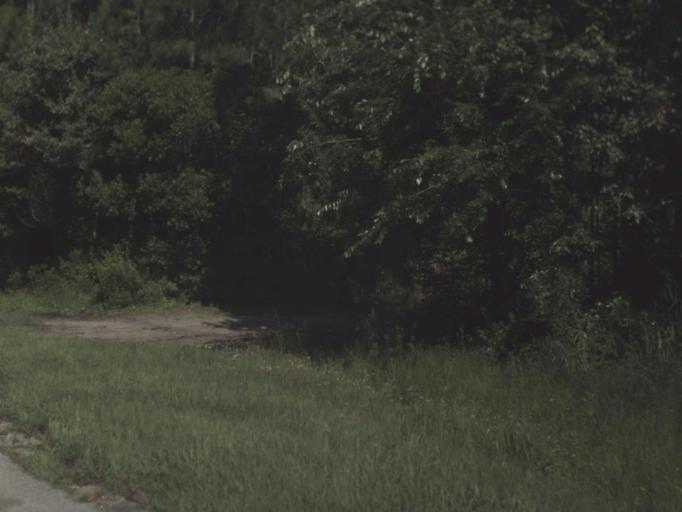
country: US
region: Florida
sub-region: Duval County
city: Baldwin
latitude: 30.3109
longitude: -81.8811
